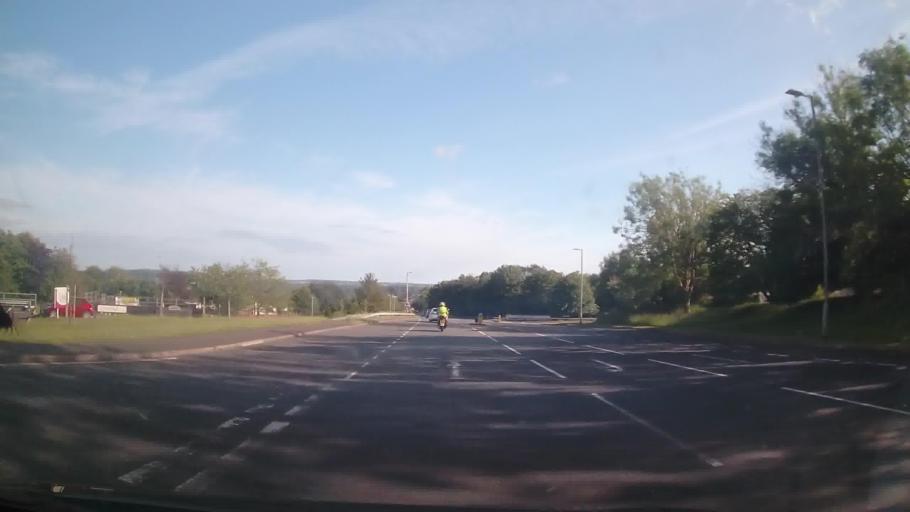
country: GB
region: England
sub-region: Devon
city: Plympton
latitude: 50.4133
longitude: -4.0949
